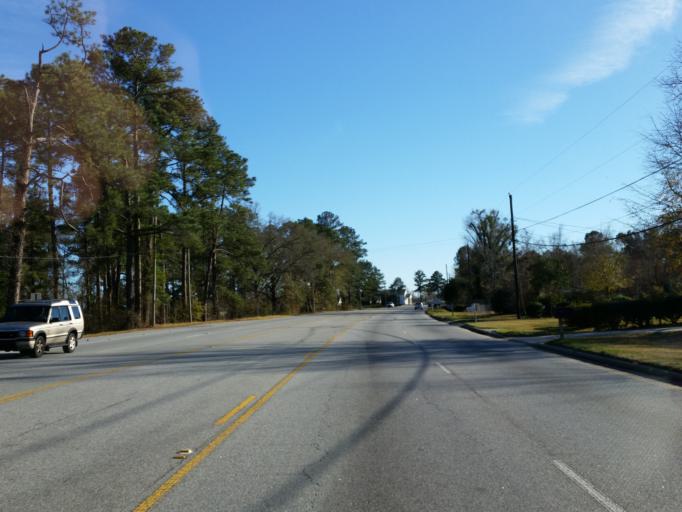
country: US
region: Georgia
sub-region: Lowndes County
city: Valdosta
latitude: 30.7670
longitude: -83.2675
